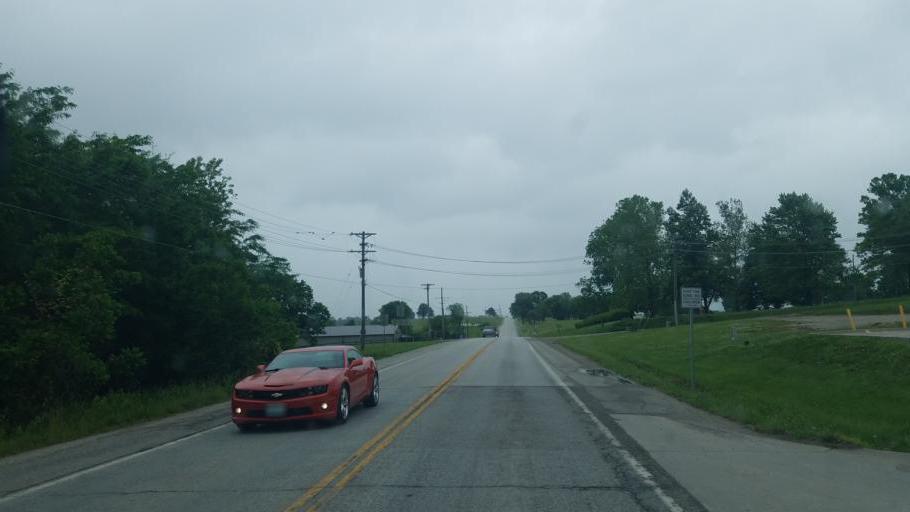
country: US
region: Missouri
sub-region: Carroll County
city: Carrollton
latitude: 39.3762
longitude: -93.4849
